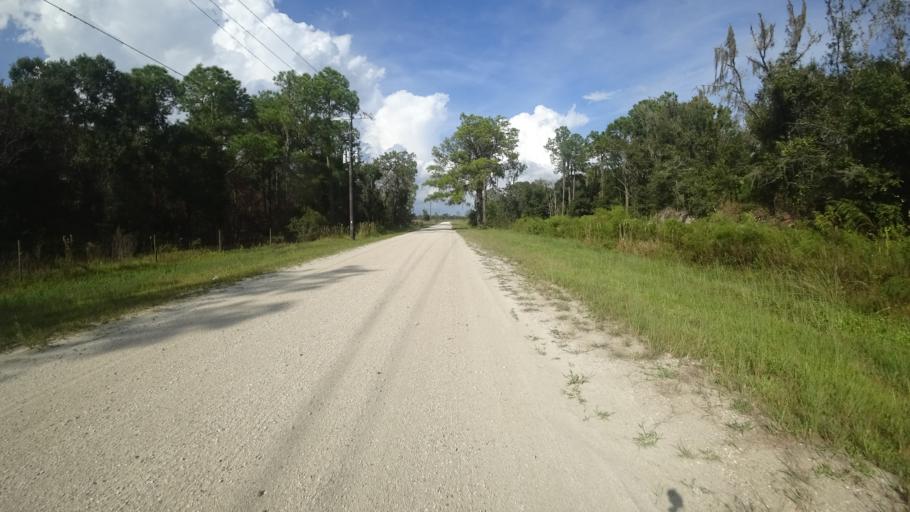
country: US
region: Florida
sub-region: Hillsborough County
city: Wimauma
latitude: 27.5913
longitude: -82.1229
